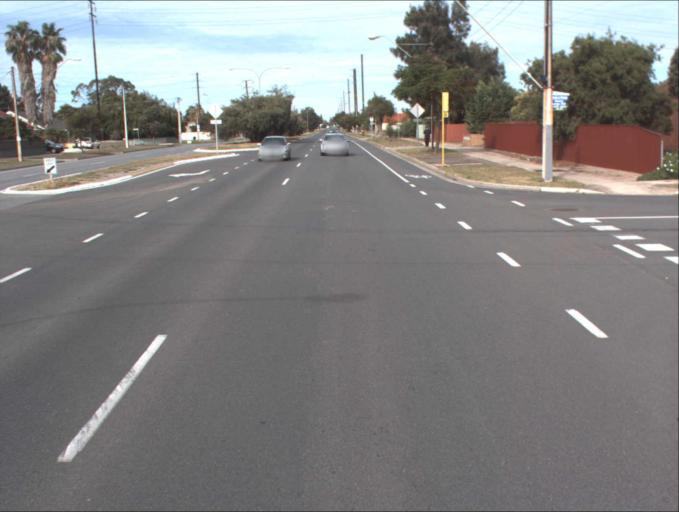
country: AU
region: South Australia
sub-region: Port Adelaide Enfield
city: Birkenhead
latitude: -34.7961
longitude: 138.5013
